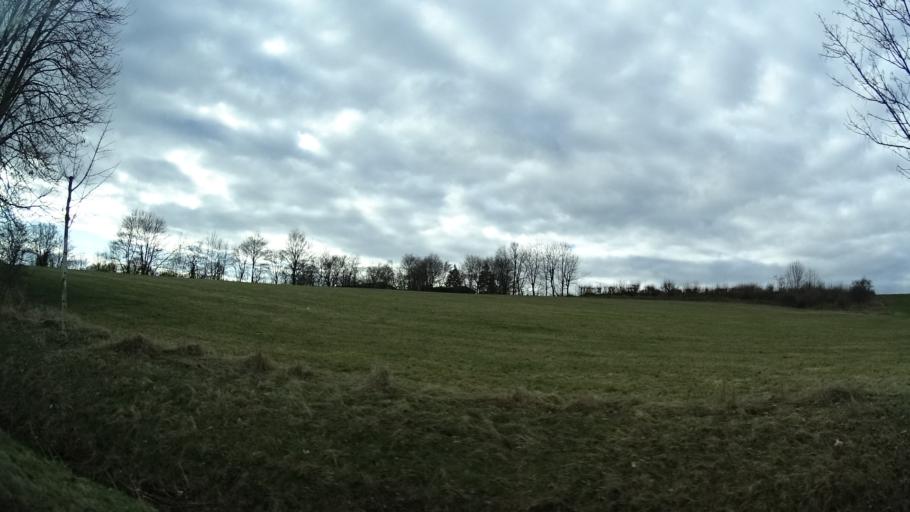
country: DE
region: Hesse
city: Gedern
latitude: 50.4340
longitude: 9.2001
